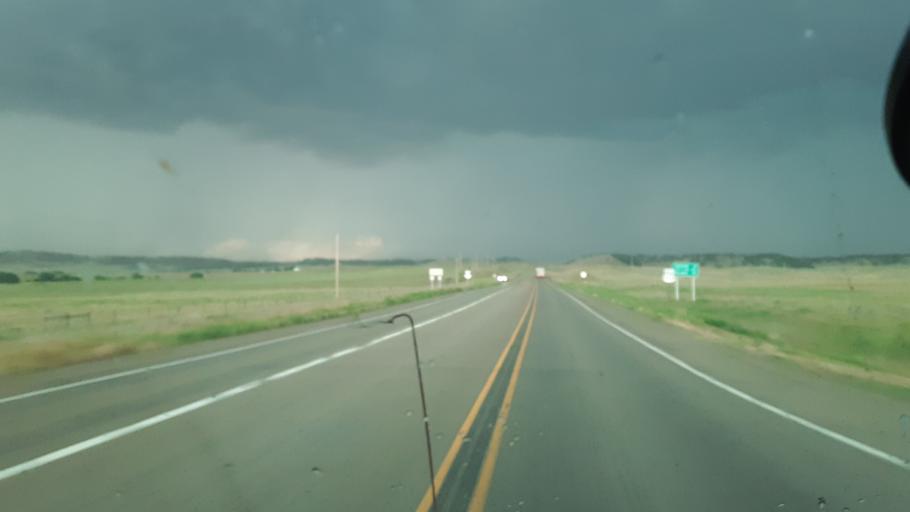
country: US
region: Montana
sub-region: Powder River County
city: Broadus
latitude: 45.4660
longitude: -105.4624
